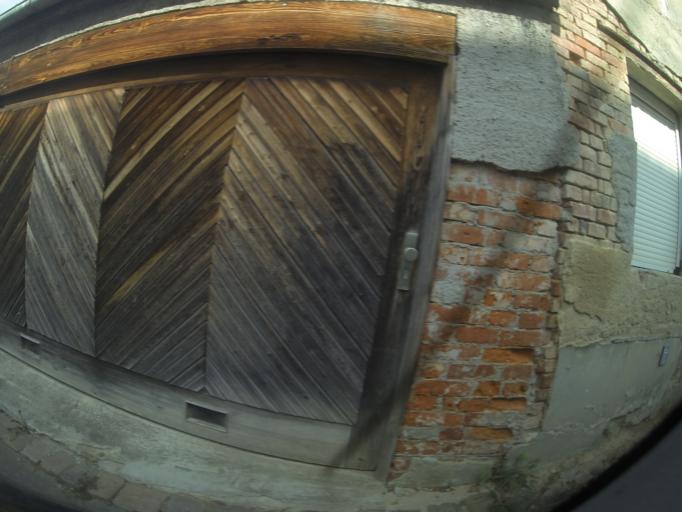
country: DE
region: Thuringia
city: Schmolln
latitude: 50.8964
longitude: 12.3565
